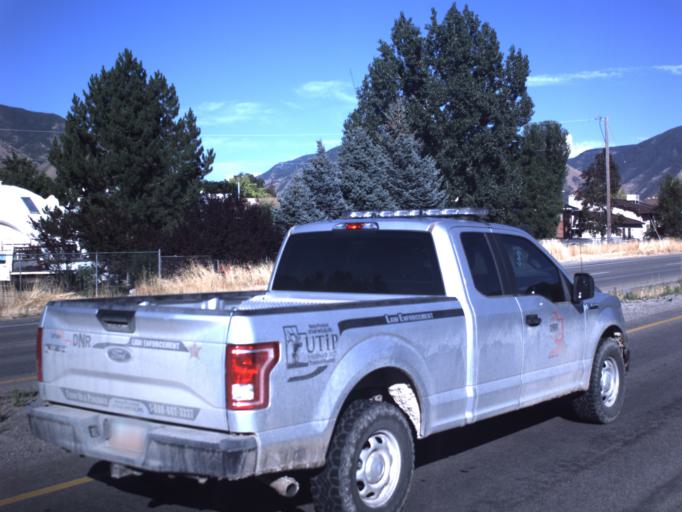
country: US
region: Utah
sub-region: Utah County
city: Springville
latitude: 40.1544
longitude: -111.6092
